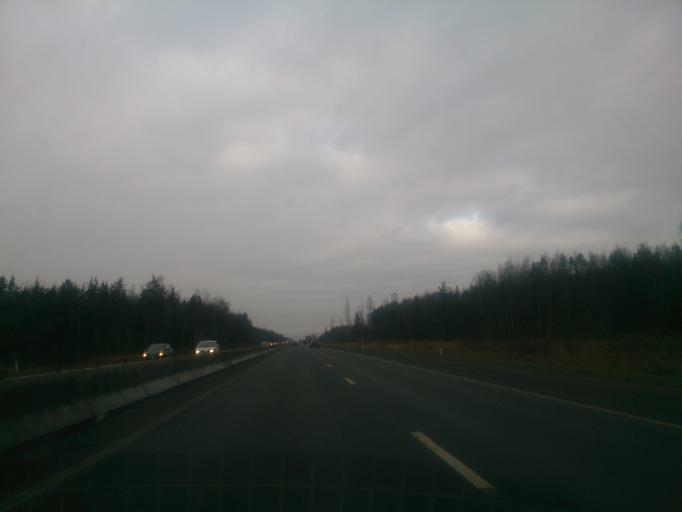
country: RU
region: Leningrad
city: Krasnyy Bor
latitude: 59.6500
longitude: 30.6777
